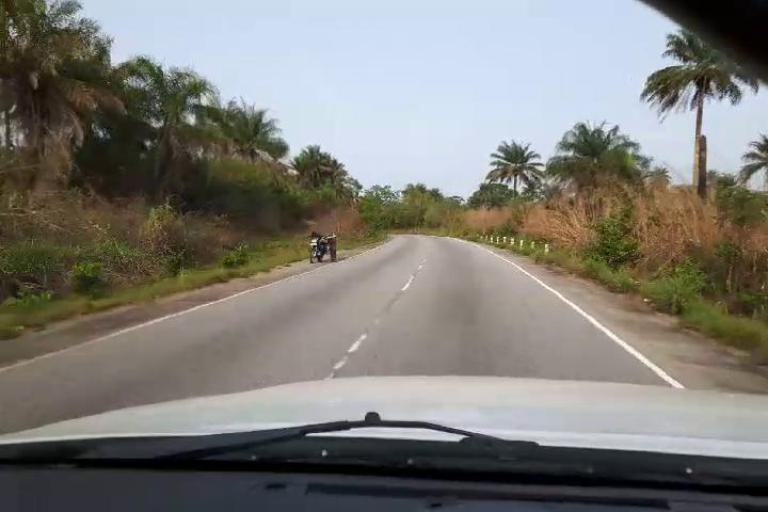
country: SL
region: Southern Province
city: Baoma
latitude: 7.9267
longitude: -11.5339
